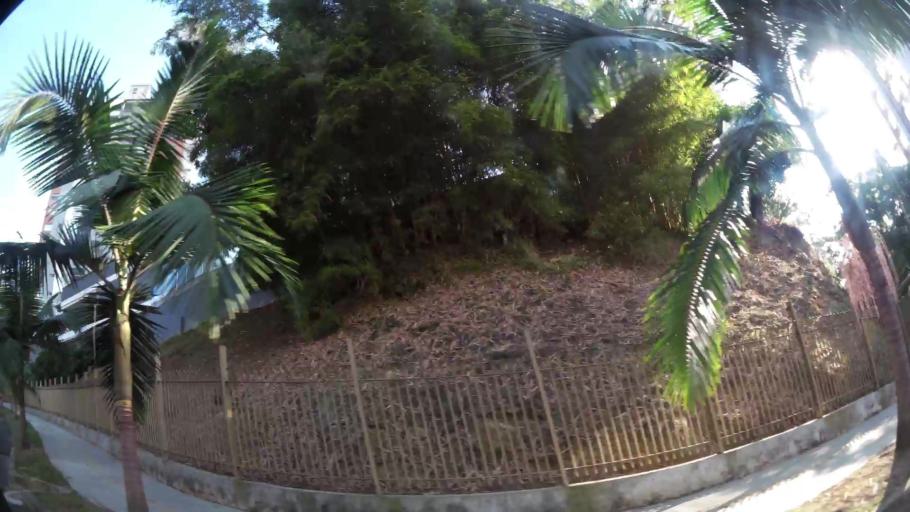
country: CO
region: Antioquia
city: Medellin
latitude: 6.2237
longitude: -75.5663
